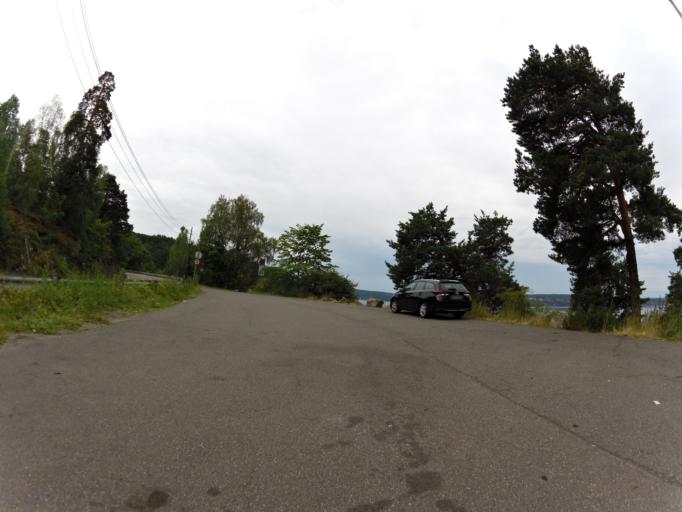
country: NO
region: Akershus
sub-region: Oppegard
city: Kolbotn
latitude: 59.8311
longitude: 10.7677
